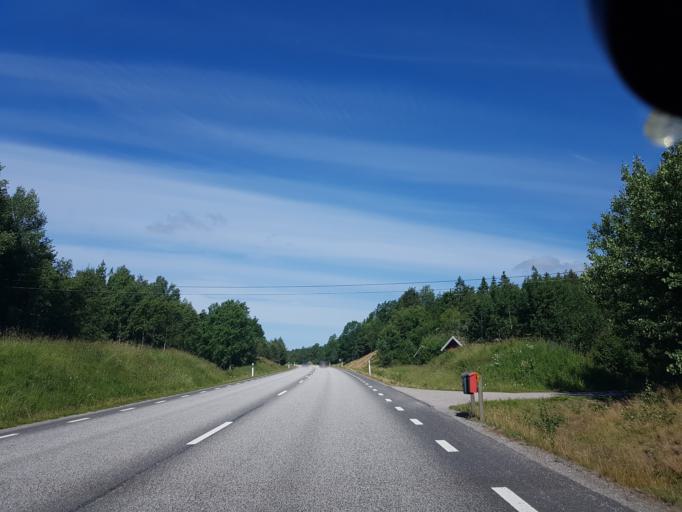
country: SE
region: Vaestra Goetaland
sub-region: Orust
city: Henan
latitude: 58.1447
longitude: 11.6359
